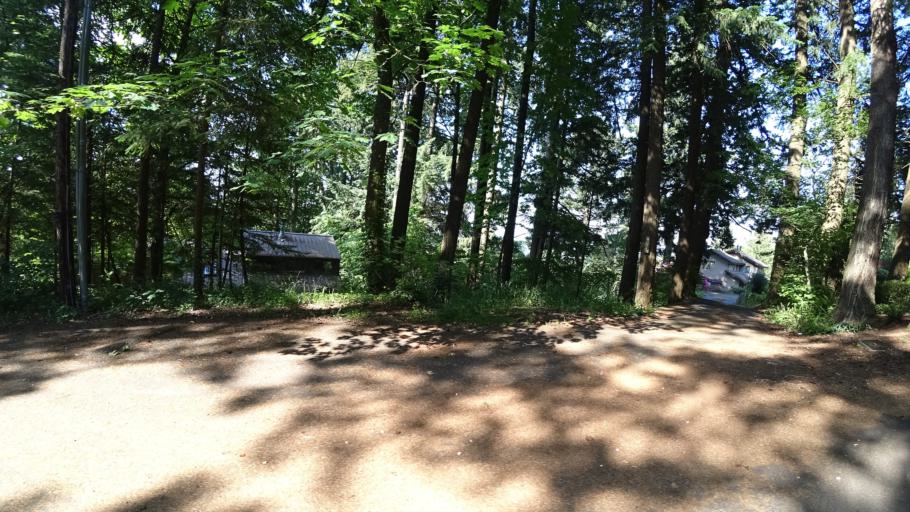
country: US
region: Oregon
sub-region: Washington County
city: West Slope
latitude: 45.4993
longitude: -122.7239
